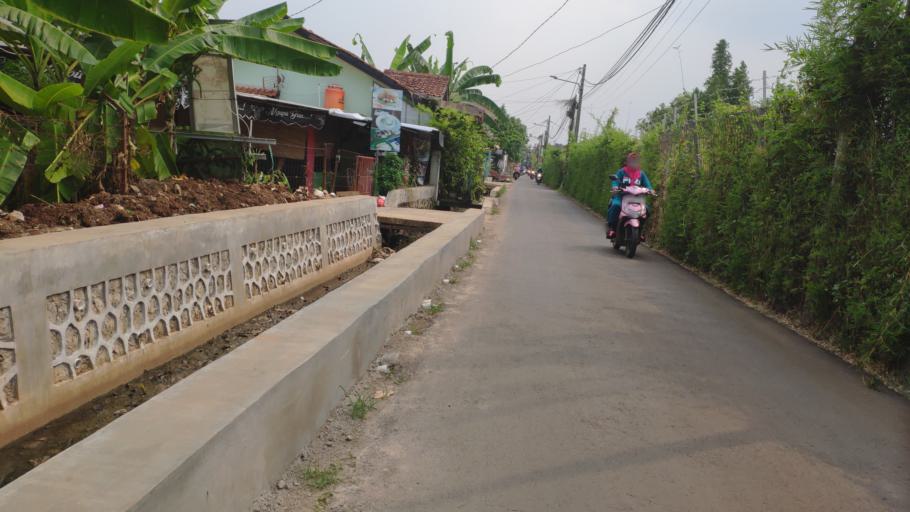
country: ID
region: West Java
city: Depok
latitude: -6.3405
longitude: 106.8166
